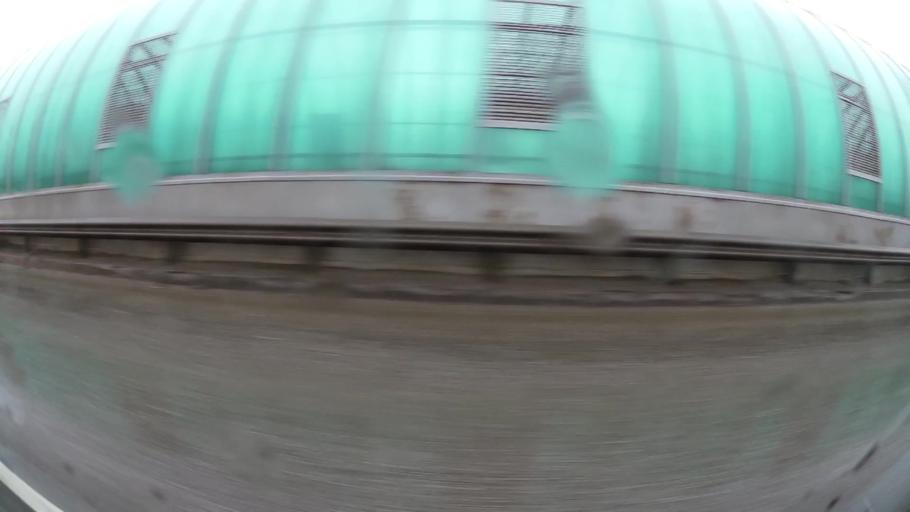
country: BG
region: Sofia-Capital
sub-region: Stolichna Obshtina
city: Sofia
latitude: 42.6568
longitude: 23.3674
